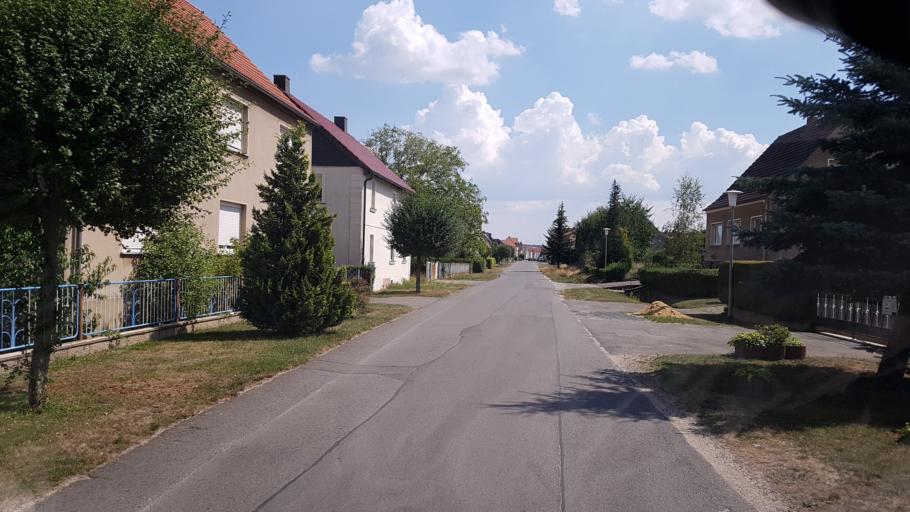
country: DE
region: Brandenburg
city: Hirschfeld
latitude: 51.3926
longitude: 13.6156
